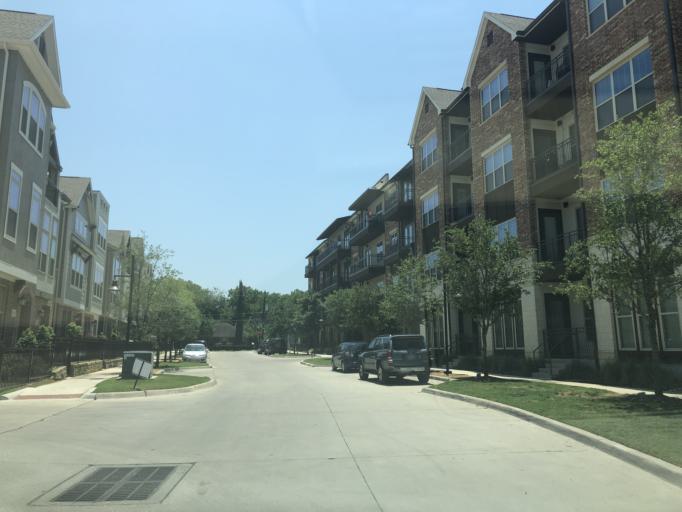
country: US
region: Texas
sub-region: Dallas County
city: Dallas
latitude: 32.7773
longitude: -96.8409
